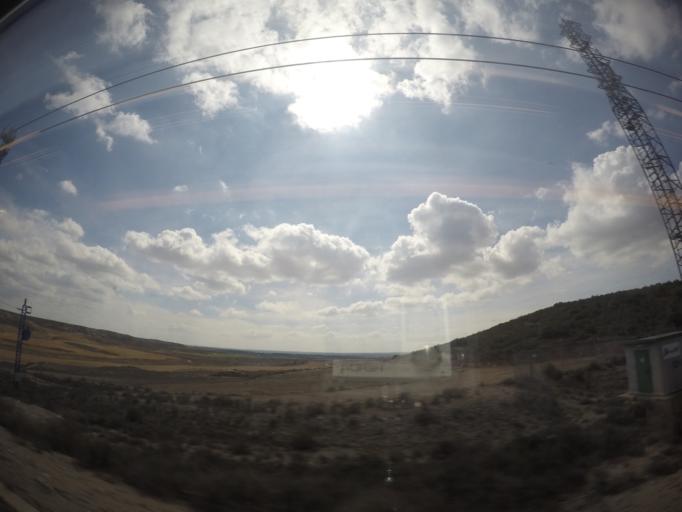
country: ES
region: Aragon
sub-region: Provincia de Huesca
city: Candasnos
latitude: 41.5553
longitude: 0.0725
